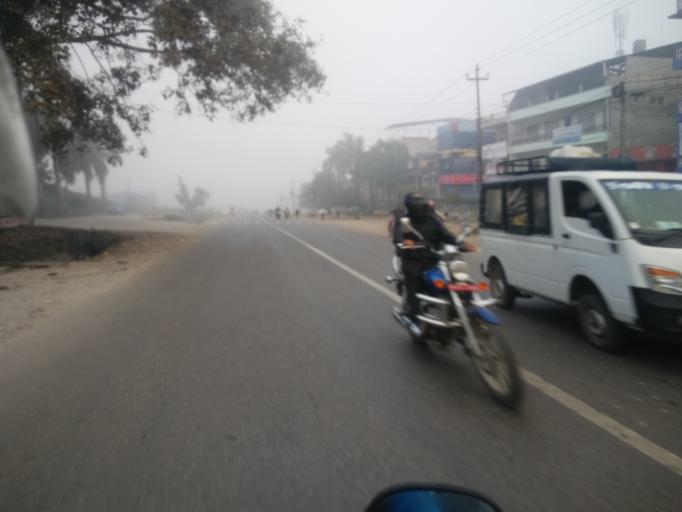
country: NP
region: Central Region
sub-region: Narayani Zone
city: Bharatpur
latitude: 27.6882
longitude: 84.4282
